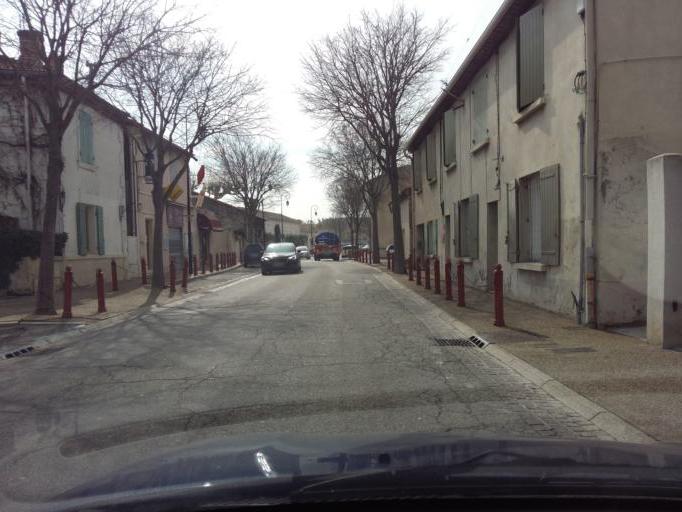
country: FR
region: Provence-Alpes-Cote d'Azur
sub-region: Departement des Bouches-du-Rhone
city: Noves
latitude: 43.8777
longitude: 4.9026
